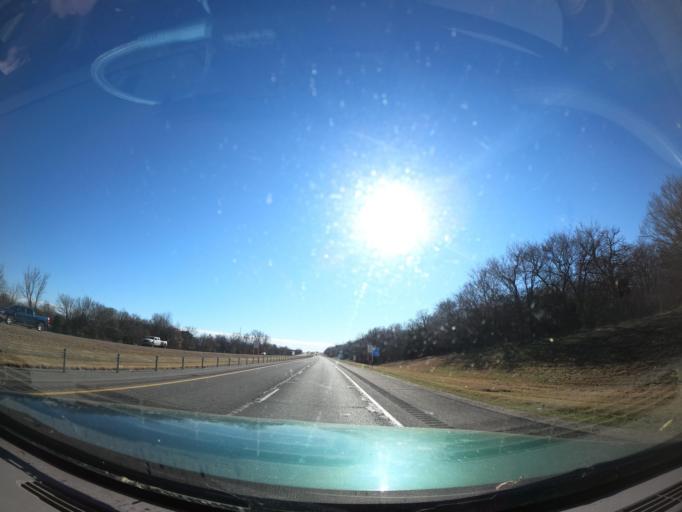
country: US
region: Oklahoma
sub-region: McIntosh County
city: Eufaula
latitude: 35.3727
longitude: -95.5713
